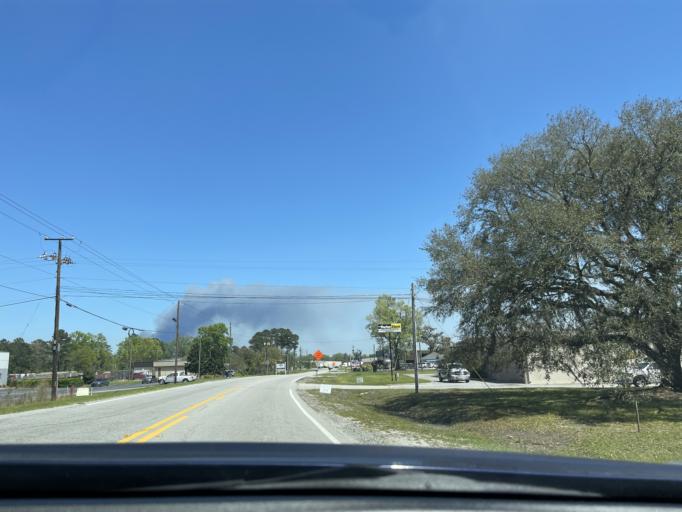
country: US
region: Georgia
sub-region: Chatham County
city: Pooler
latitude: 32.0995
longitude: -81.2266
